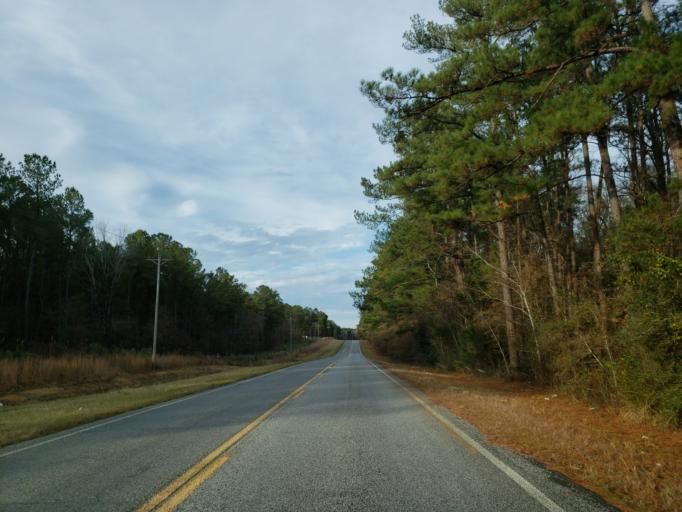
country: US
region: Mississippi
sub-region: Wayne County
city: Waynesboro
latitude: 31.8314
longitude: -88.6897
